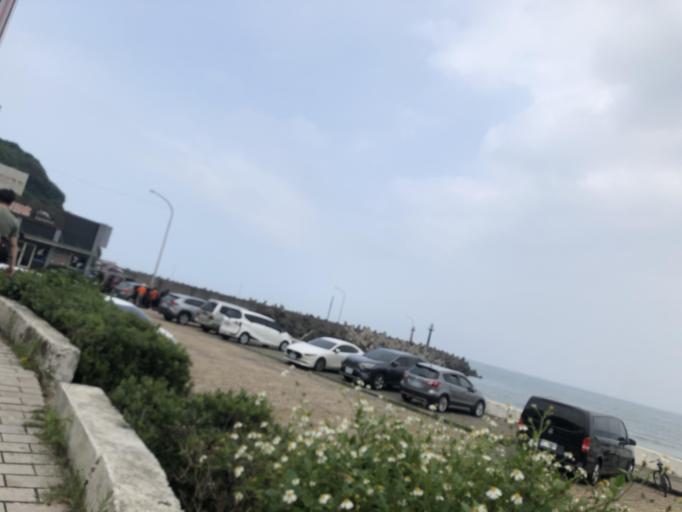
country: TW
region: Taiwan
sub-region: Keelung
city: Keelung
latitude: 25.2248
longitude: 121.6497
